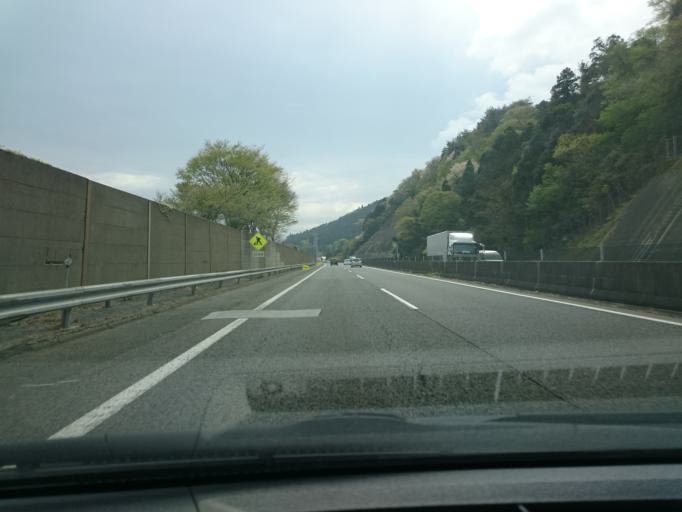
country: JP
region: Shiga Prefecture
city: Nagahama
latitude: 35.3335
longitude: 136.3728
